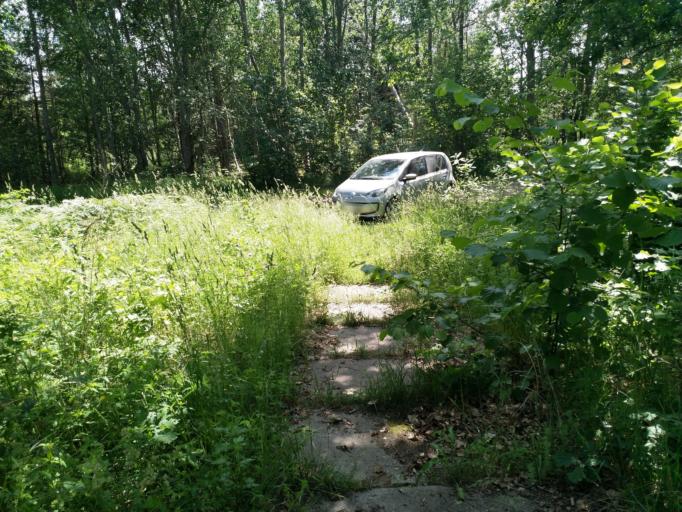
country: LV
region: Kuldigas Rajons
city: Kuldiga
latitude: 56.9698
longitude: 21.9135
